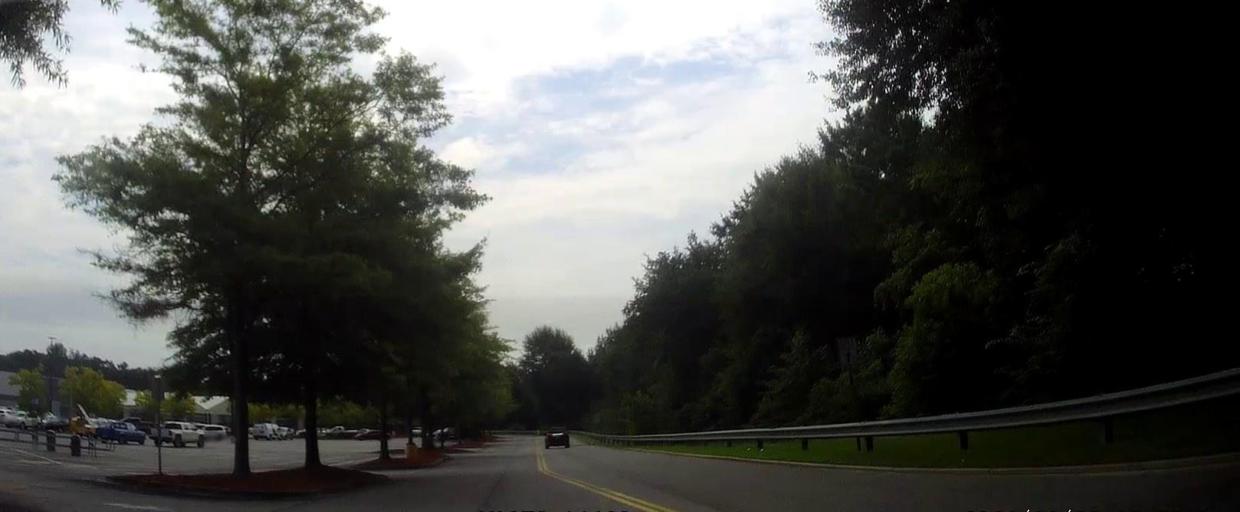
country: US
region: Georgia
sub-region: Bibb County
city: West Point
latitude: 32.8091
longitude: -83.7199
